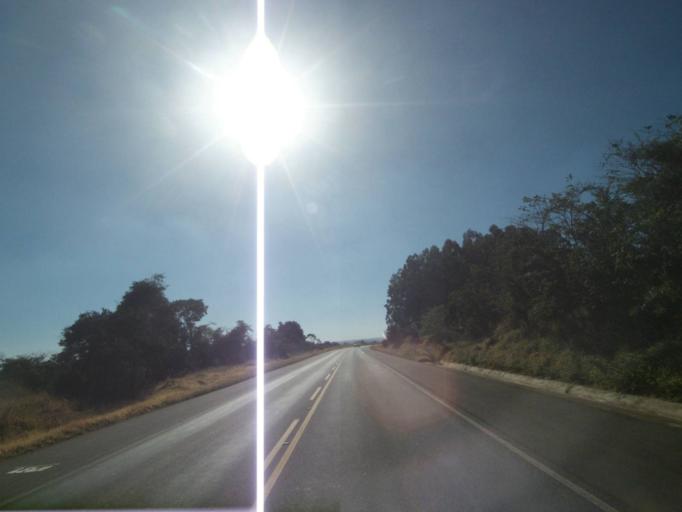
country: BR
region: Parana
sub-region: Tibagi
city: Tibagi
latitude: -24.7647
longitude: -50.4693
